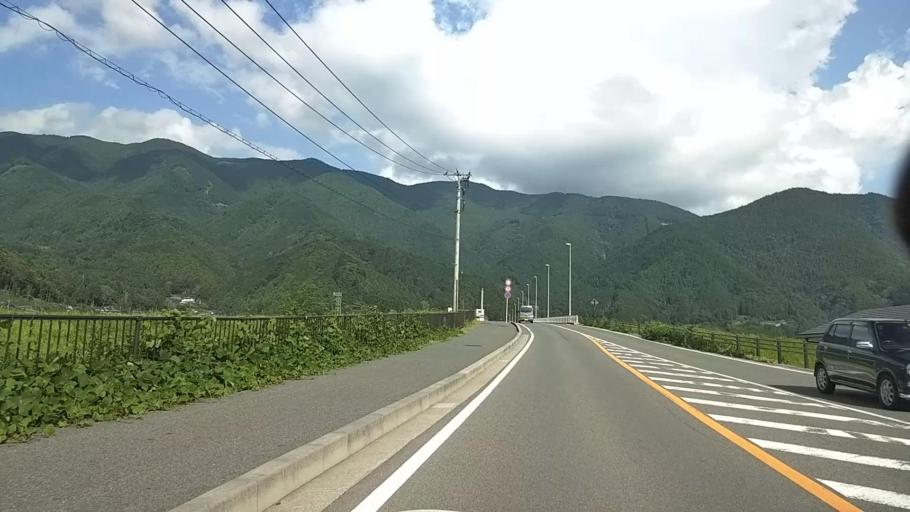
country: JP
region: Shizuoka
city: Fujinomiya
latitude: 35.2820
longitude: 138.4570
